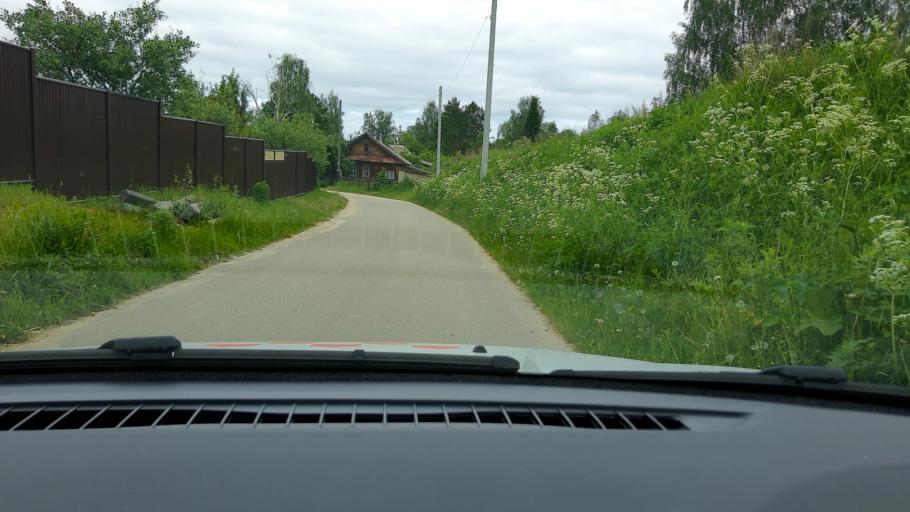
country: RU
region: Nizjnij Novgorod
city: Sitniki
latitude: 56.5181
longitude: 44.1149
